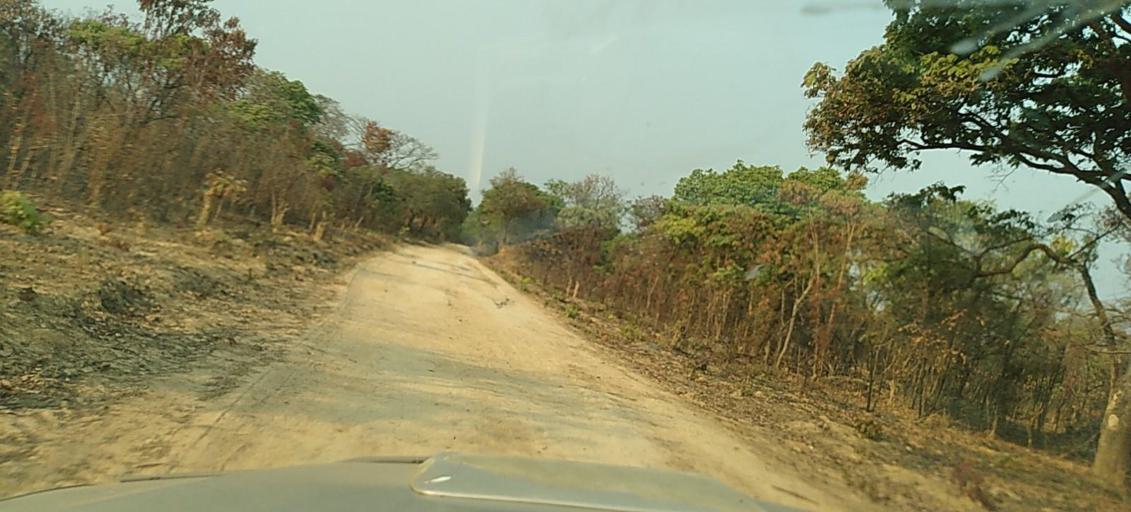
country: ZM
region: North-Western
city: Kasempa
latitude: -13.2689
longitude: 26.5596
